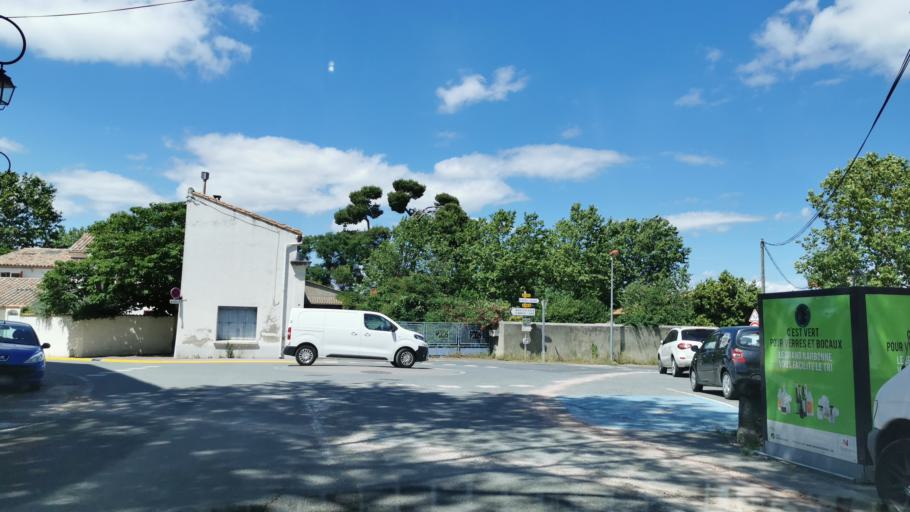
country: FR
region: Languedoc-Roussillon
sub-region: Departement de l'Aude
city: Moussan
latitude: 43.2321
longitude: 2.9505
